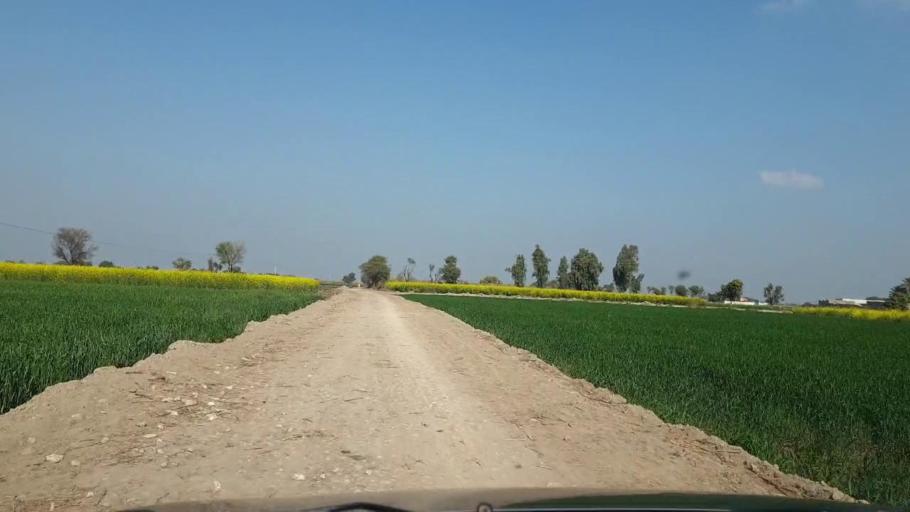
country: PK
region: Sindh
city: Sinjhoro
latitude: 26.0536
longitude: 68.7294
